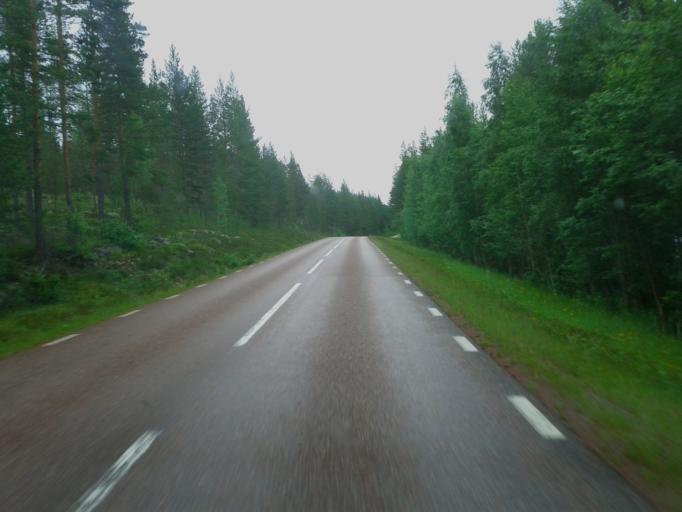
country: NO
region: Hedmark
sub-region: Trysil
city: Innbygda
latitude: 61.7836
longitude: 12.9363
